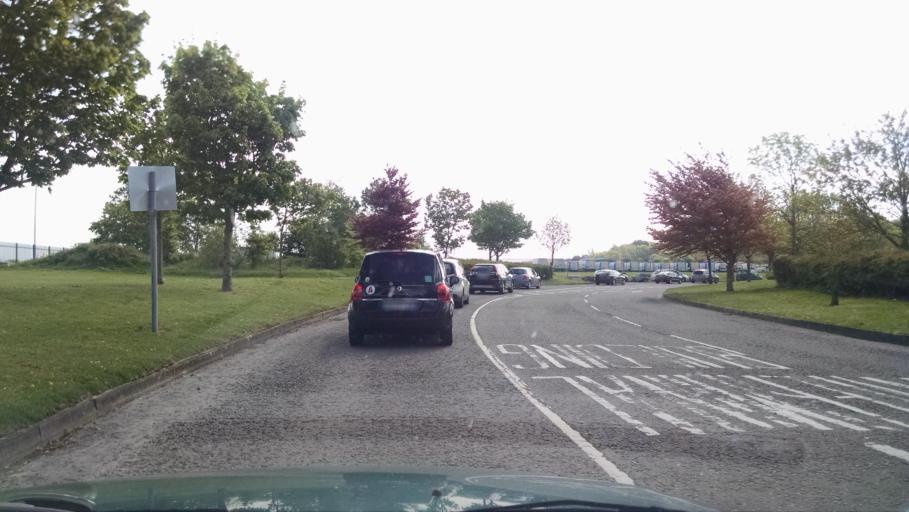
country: IE
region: Munster
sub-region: County Cork
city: Cobh
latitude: 51.8326
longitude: -8.3172
